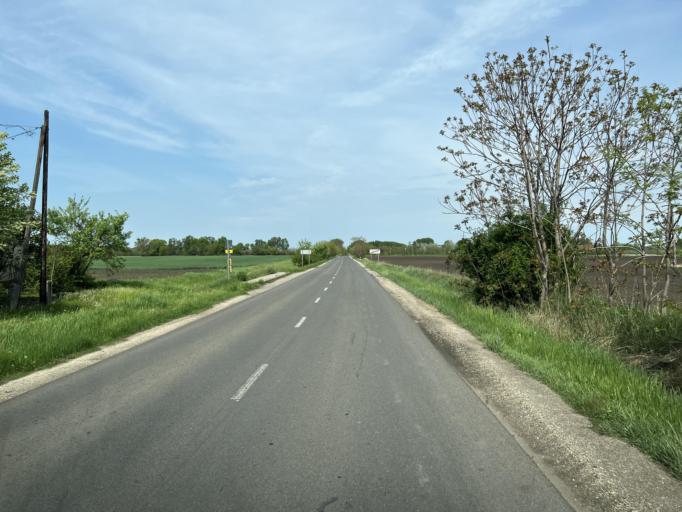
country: HU
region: Pest
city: Abony
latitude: 47.2018
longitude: 19.9948
